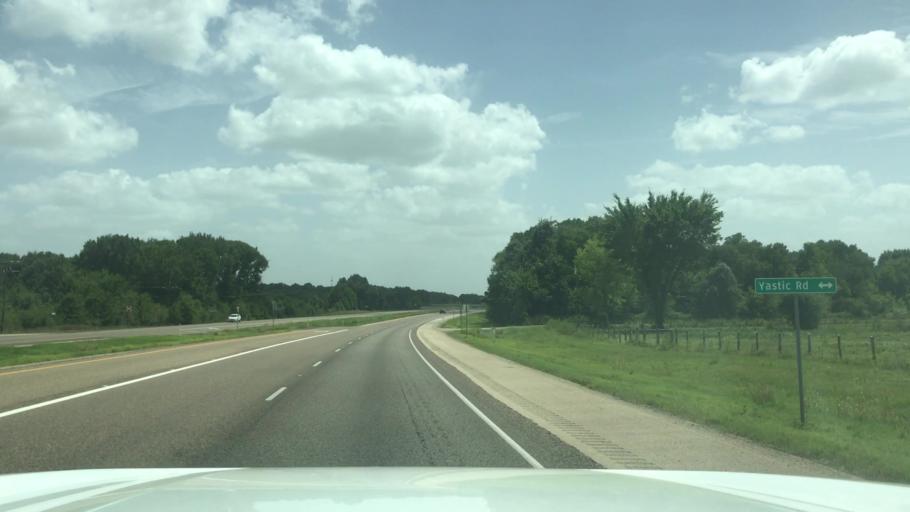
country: US
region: Texas
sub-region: Robertson County
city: Calvert
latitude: 31.1204
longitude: -96.7123
